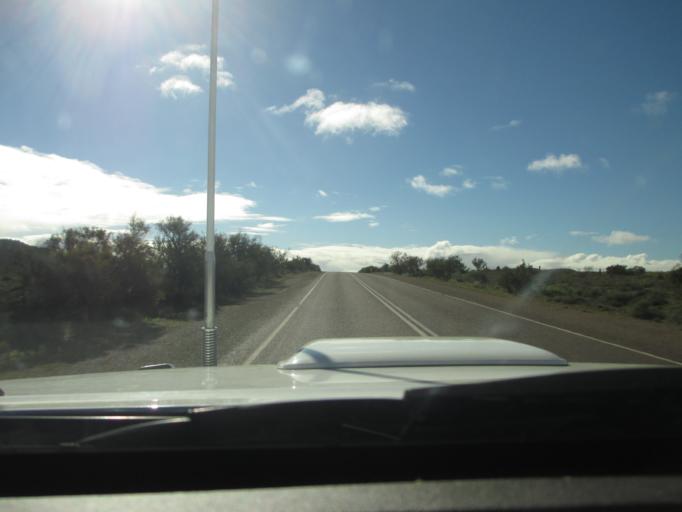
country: AU
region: South Australia
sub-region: Flinders Ranges
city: Quorn
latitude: -31.9353
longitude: 138.4115
